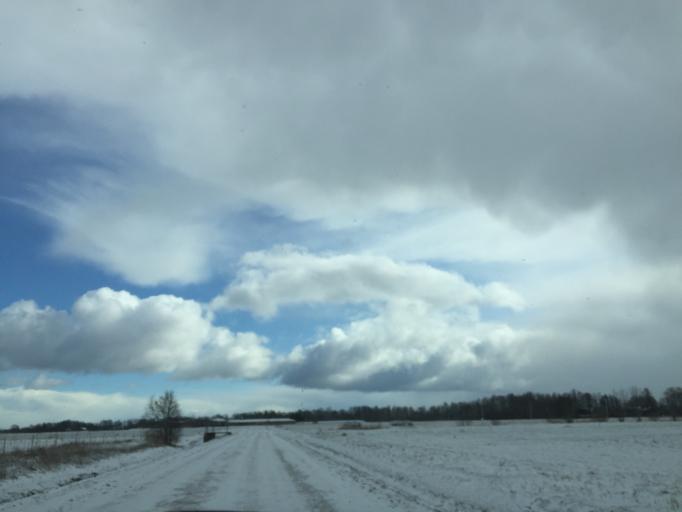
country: LV
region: Ventspils
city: Ventspils
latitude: 57.3731
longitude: 21.6237
